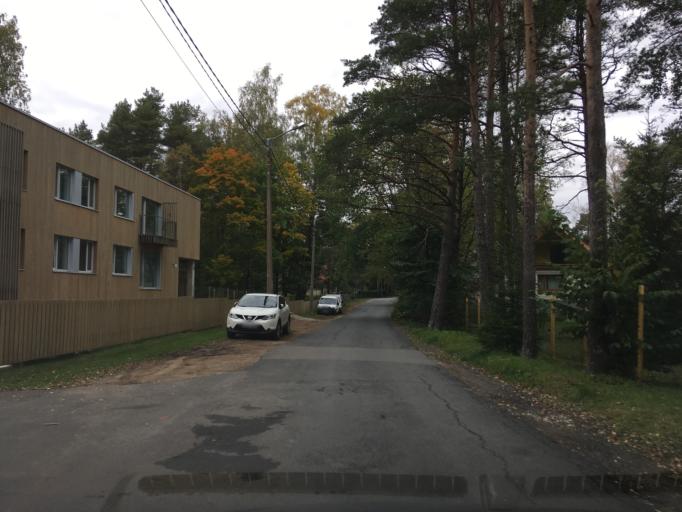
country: EE
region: Harju
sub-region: Tallinna linn
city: Tallinn
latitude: 59.3711
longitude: 24.7135
